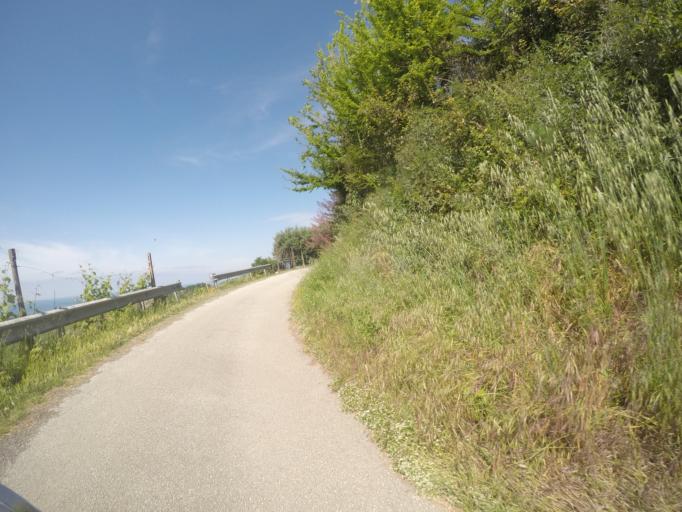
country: IT
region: Tuscany
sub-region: Provincia di Massa-Carrara
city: Massa
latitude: 44.0496
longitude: 10.1022
